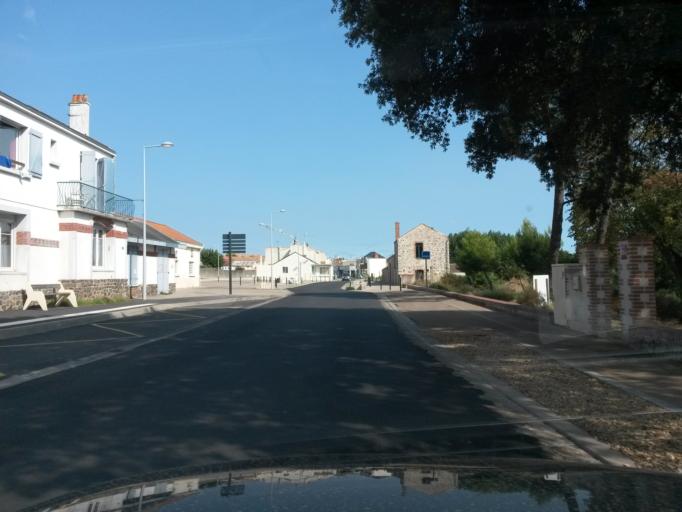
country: FR
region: Pays de la Loire
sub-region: Departement de la Vendee
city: Bretignolles-sur-Mer
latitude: 46.6059
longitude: -1.8350
